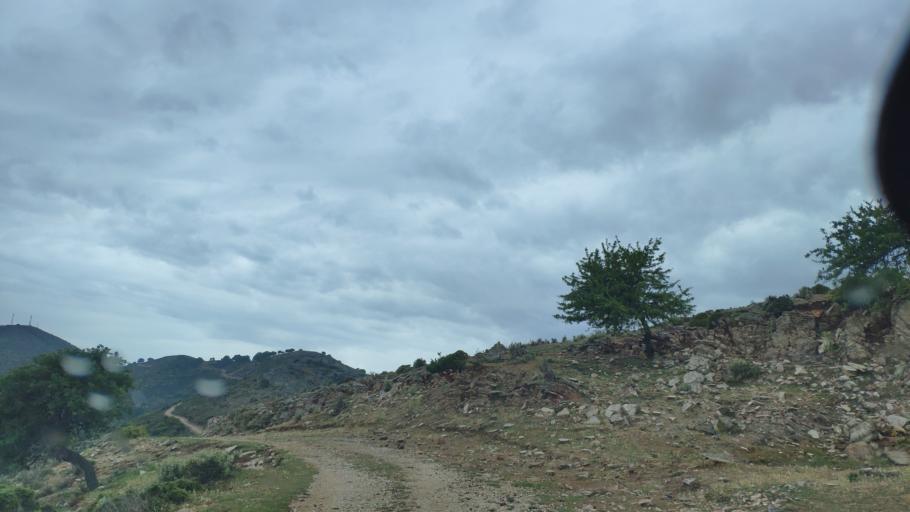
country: GR
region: West Greece
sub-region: Nomos Aitolias kai Akarnanias
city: Archontochorion
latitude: 38.6796
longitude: 21.0176
